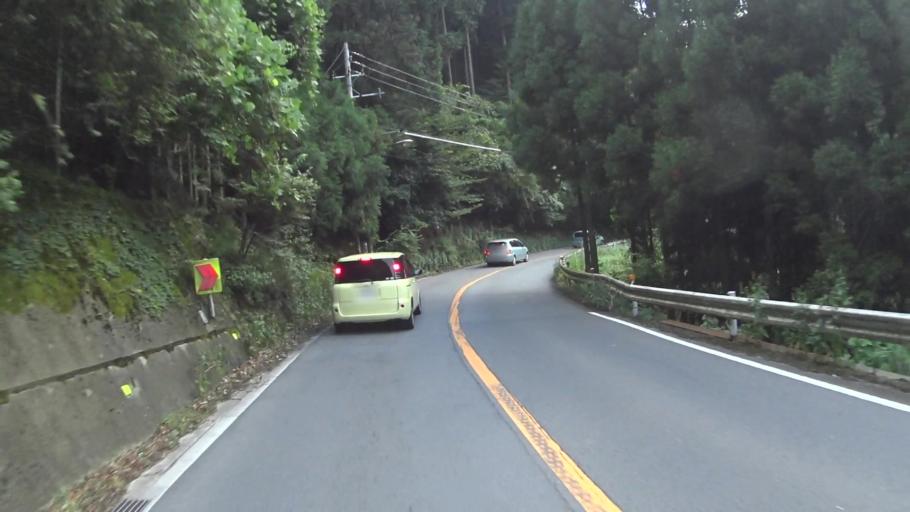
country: JP
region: Kyoto
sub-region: Kyoto-shi
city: Kamigyo-ku
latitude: 35.0715
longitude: 135.6857
